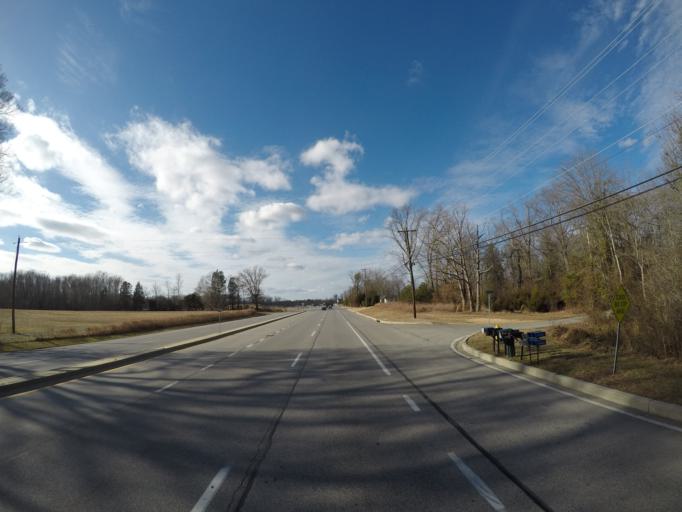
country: US
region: Maryland
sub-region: Charles County
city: Saint Charles
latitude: 38.6080
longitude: -76.9577
